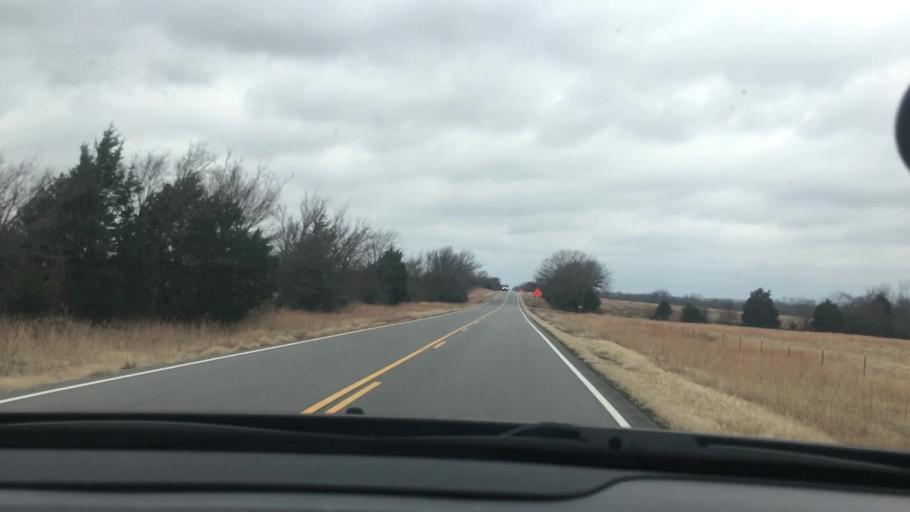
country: US
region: Oklahoma
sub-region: Atoka County
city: Atoka
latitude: 34.3749
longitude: -96.2003
